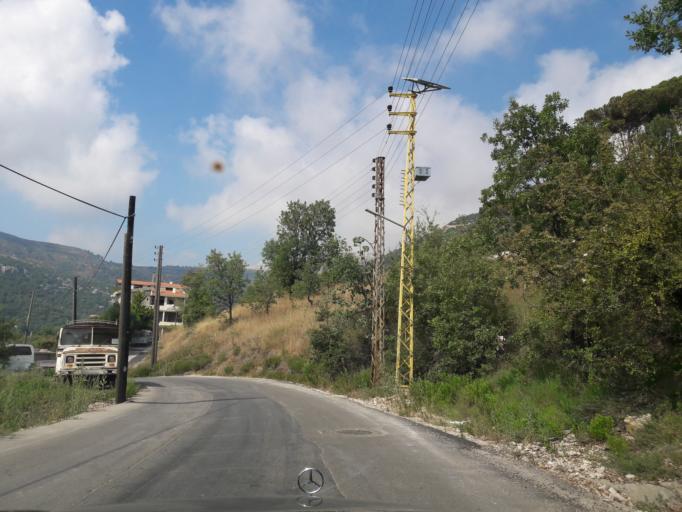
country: LB
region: Mont-Liban
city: Djounie
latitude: 33.9566
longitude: 35.7769
